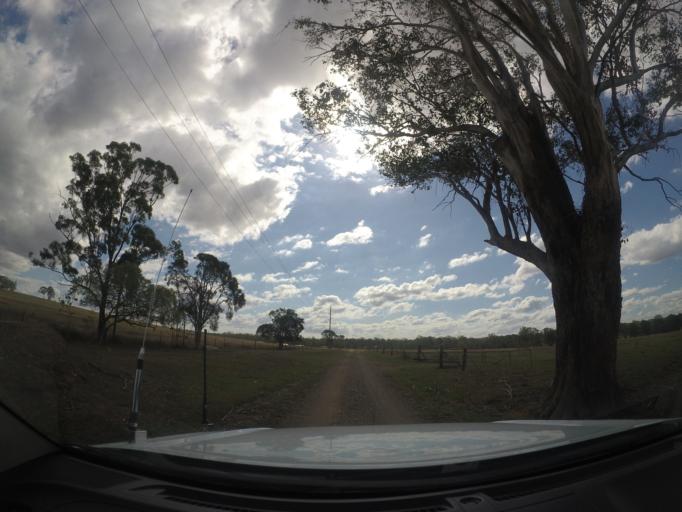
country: AU
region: Queensland
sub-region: Logan
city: North Maclean
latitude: -27.8085
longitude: 153.0027
